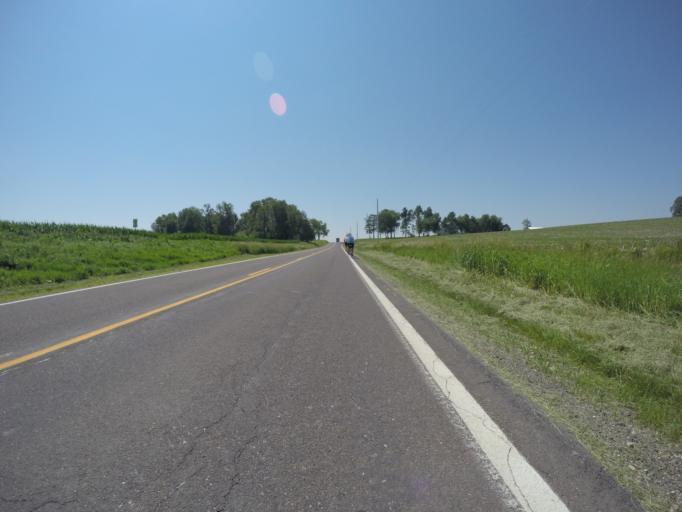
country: US
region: Kansas
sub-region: Doniphan County
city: Highland
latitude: 39.8348
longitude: -95.2653
